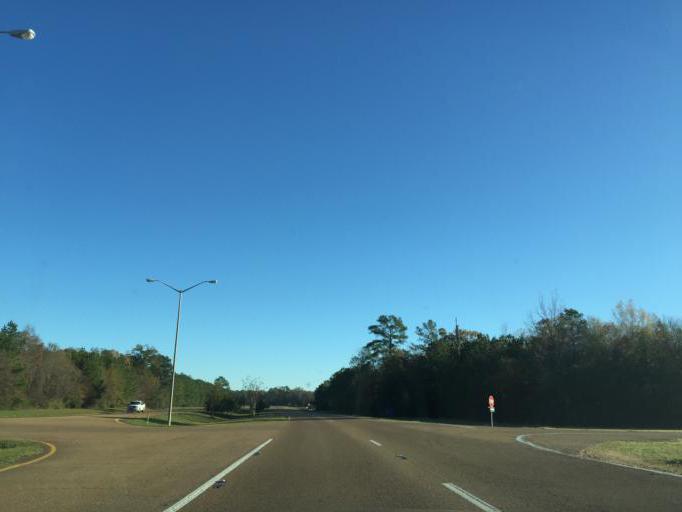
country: US
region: Mississippi
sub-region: Rankin County
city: Flowood
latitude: 32.2904
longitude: -90.1501
